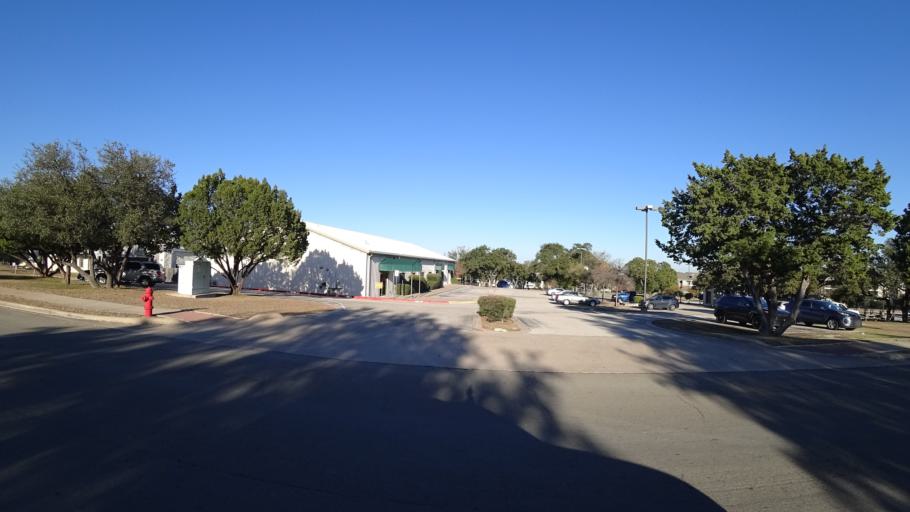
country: US
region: Texas
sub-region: Travis County
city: Wells Branch
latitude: 30.4018
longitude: -97.6993
